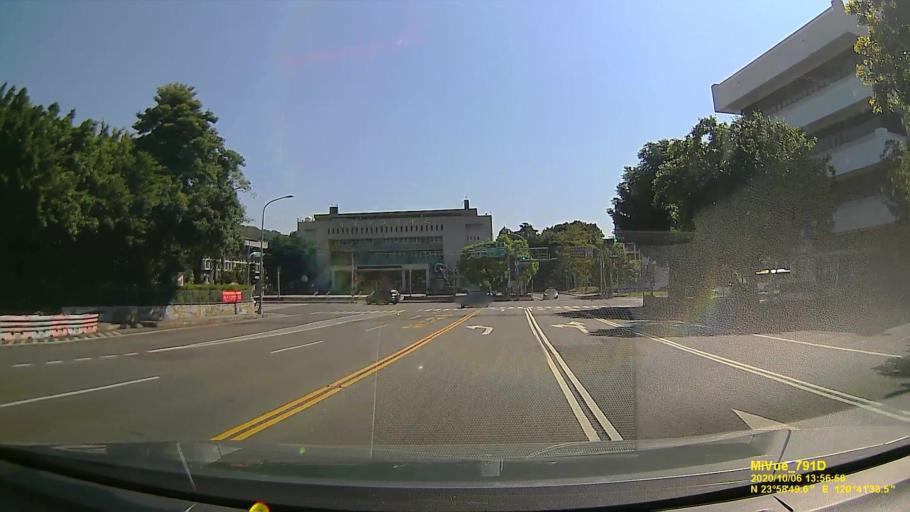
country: TW
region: Taiwan
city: Zhongxing New Village
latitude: 23.9804
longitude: 120.6926
